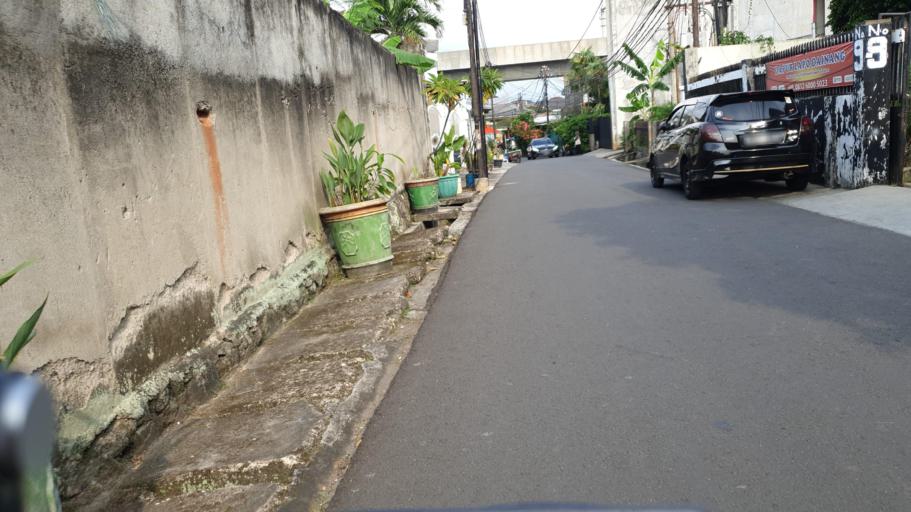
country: ID
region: Jakarta Raya
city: Jakarta
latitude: -6.2757
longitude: 106.7967
